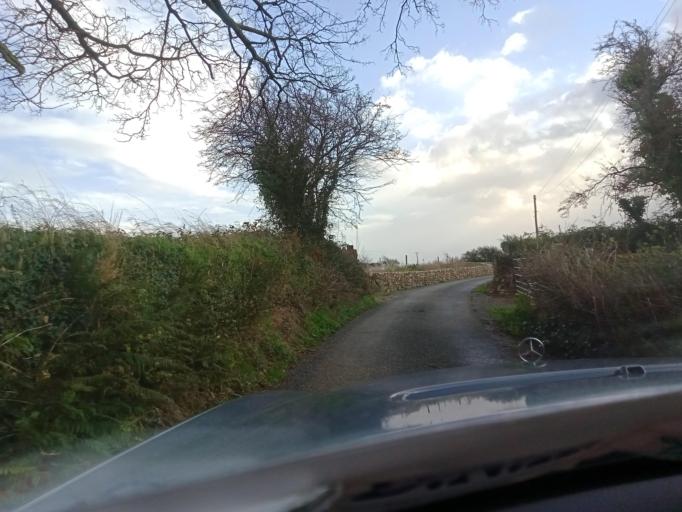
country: IE
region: Leinster
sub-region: Kilkenny
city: Mooncoin
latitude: 52.2848
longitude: -7.2657
